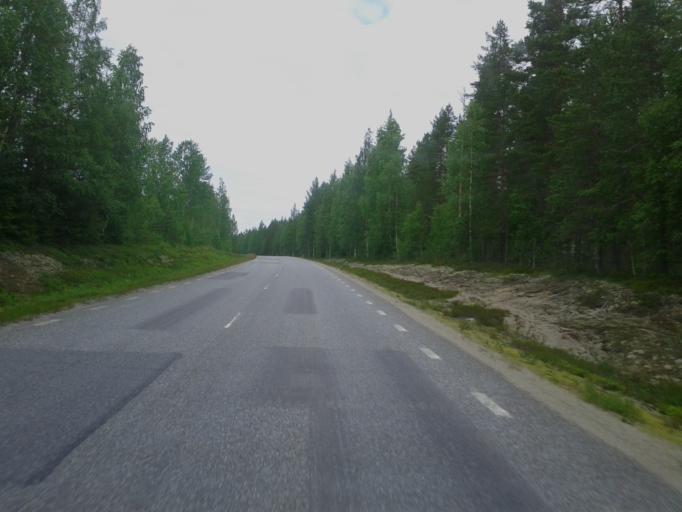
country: SE
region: Vaesternorrland
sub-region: OErnskoeldsviks Kommun
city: Bjasta
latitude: 63.2202
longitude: 18.4718
